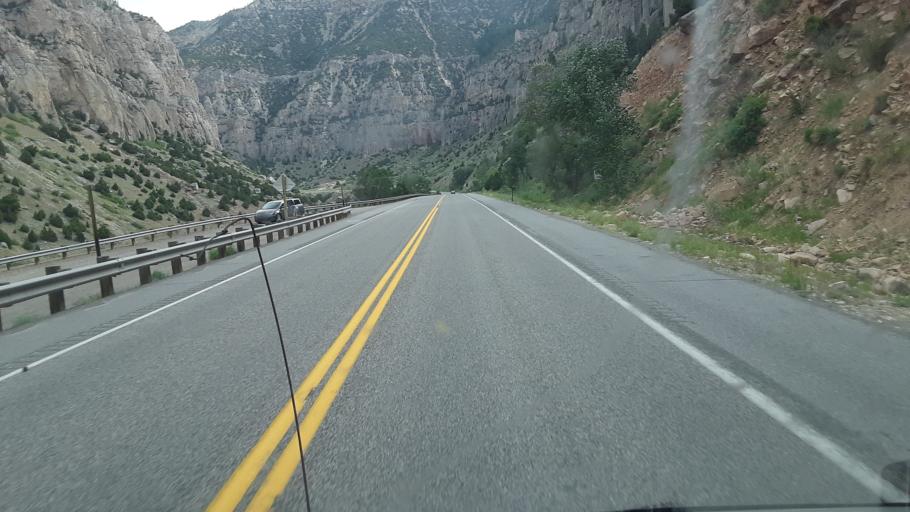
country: US
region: Wyoming
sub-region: Hot Springs County
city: Thermopolis
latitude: 43.5186
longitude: -108.1815
